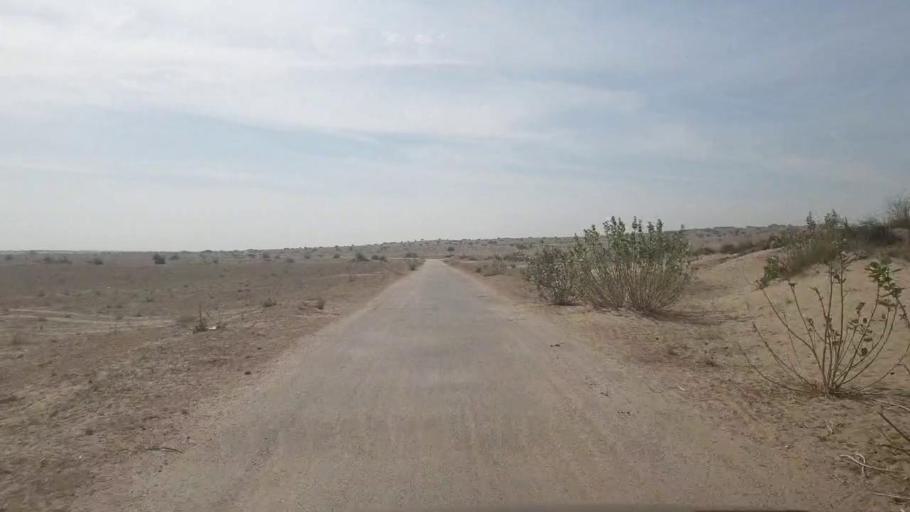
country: PK
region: Sindh
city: Umarkot
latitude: 25.2830
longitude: 69.7287
